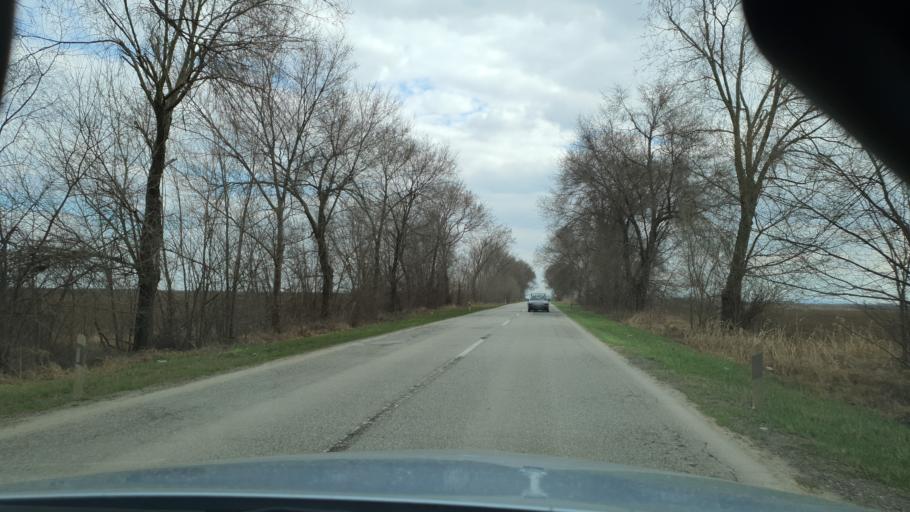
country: RS
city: Obrovac
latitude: 45.4384
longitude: 19.3734
